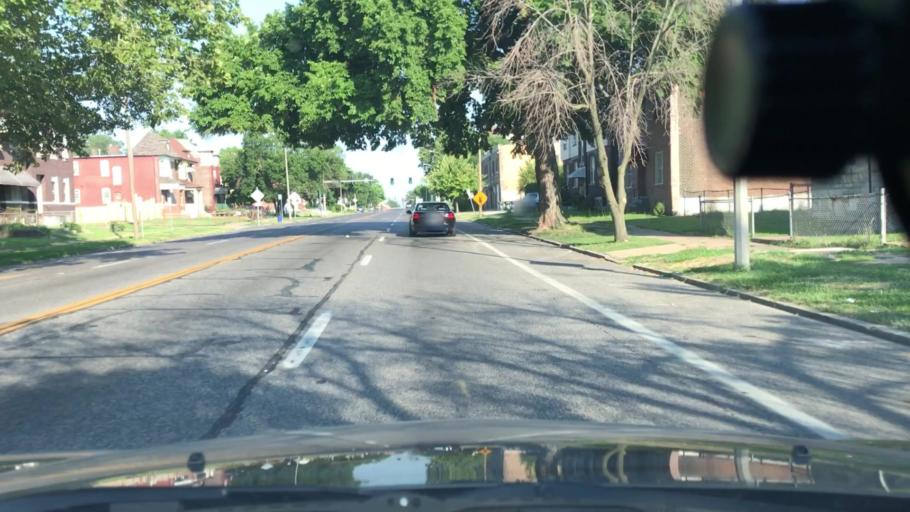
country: US
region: Missouri
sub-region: Saint Louis County
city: Hillsdale
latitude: 38.6576
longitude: -90.2540
